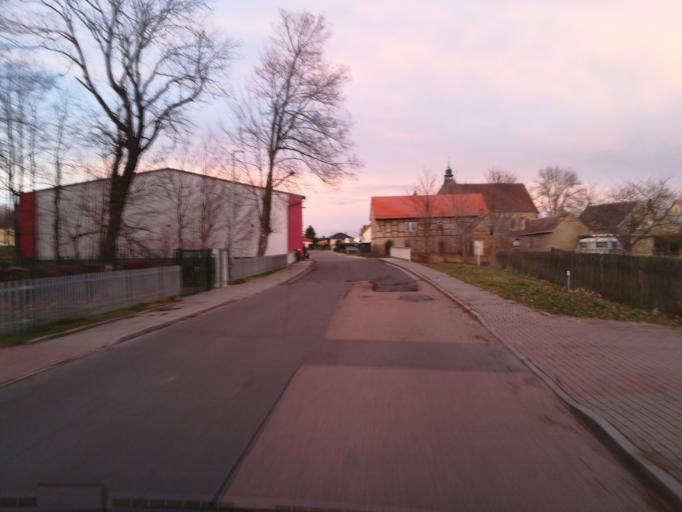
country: DE
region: Saxony-Anhalt
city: Brehna
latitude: 51.5274
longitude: 12.2272
